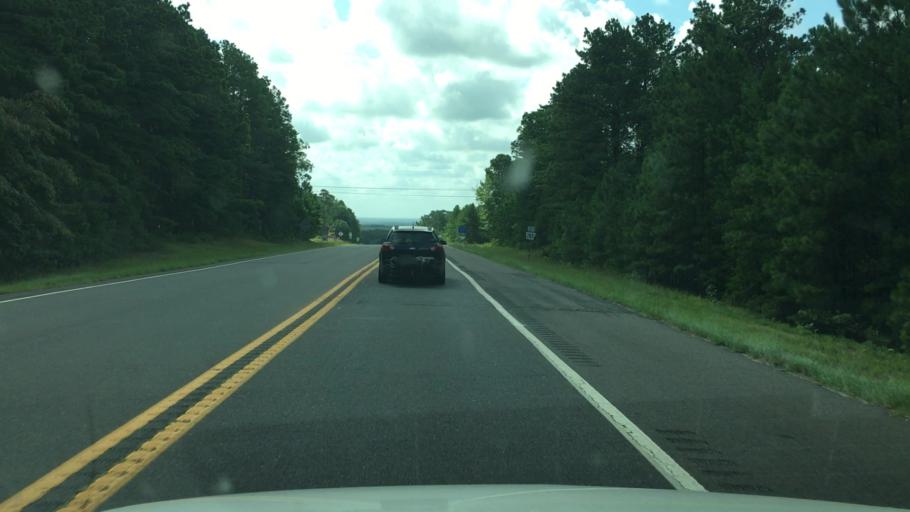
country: US
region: Arkansas
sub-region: Clark County
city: Arkadelphia
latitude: 34.2164
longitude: -93.0852
